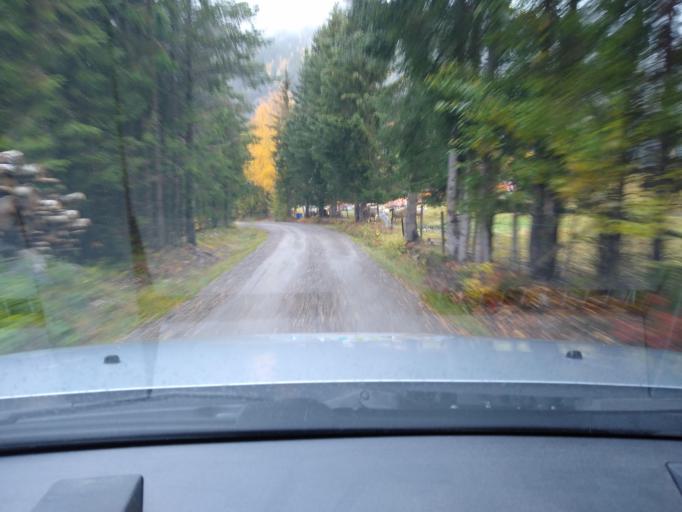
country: NO
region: Oppland
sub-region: Ringebu
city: Ringebu
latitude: 61.5530
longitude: 10.1526
